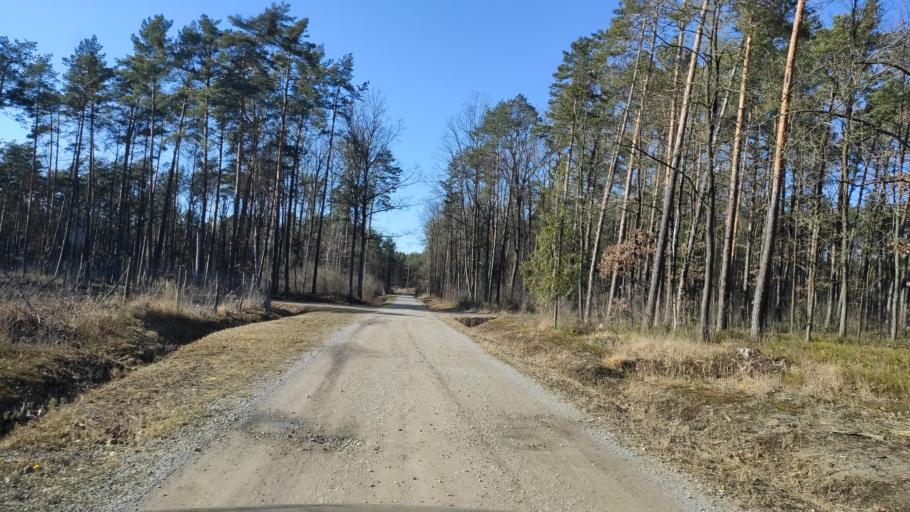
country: PL
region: Masovian Voivodeship
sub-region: Powiat radomski
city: Jedlnia-Letnisko
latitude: 51.4721
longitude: 21.3007
